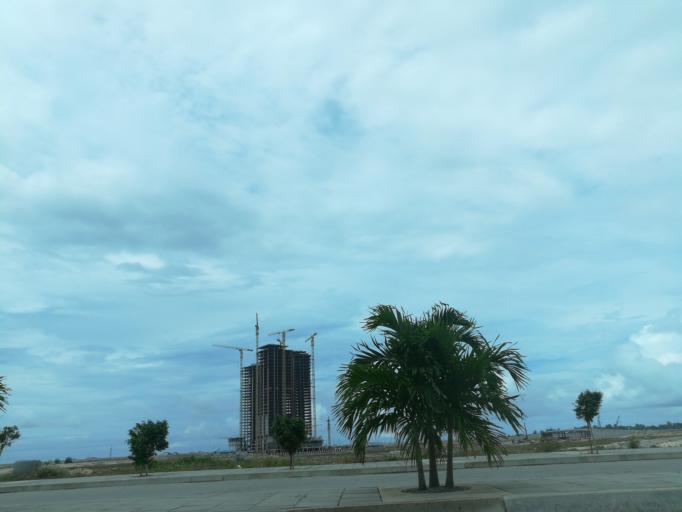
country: NG
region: Lagos
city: Lagos
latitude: 6.4088
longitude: 3.4098
